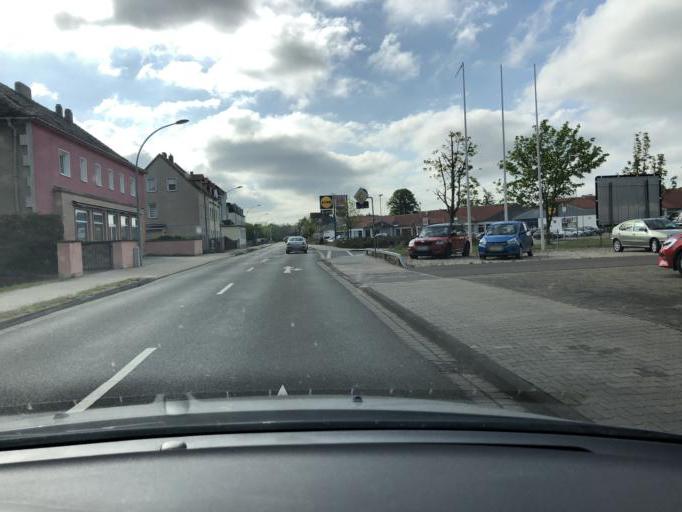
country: DE
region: Saxony
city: Bohlen
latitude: 51.1999
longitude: 12.3904
